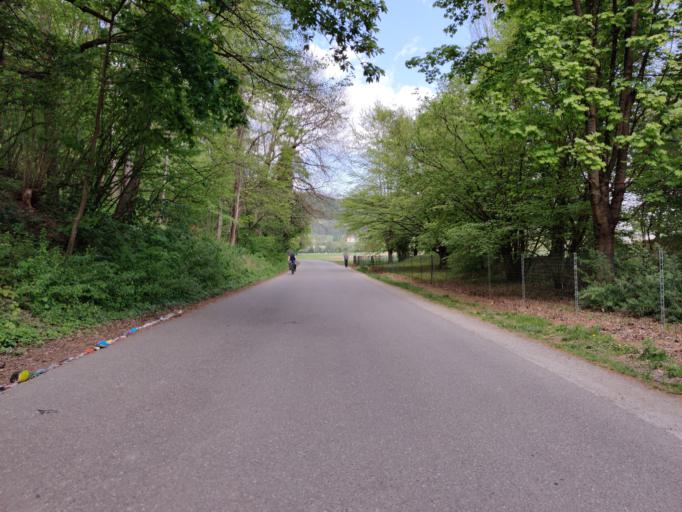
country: AT
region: Styria
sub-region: Graz Stadt
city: Wetzelsdorf
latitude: 47.0357
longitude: 15.3921
